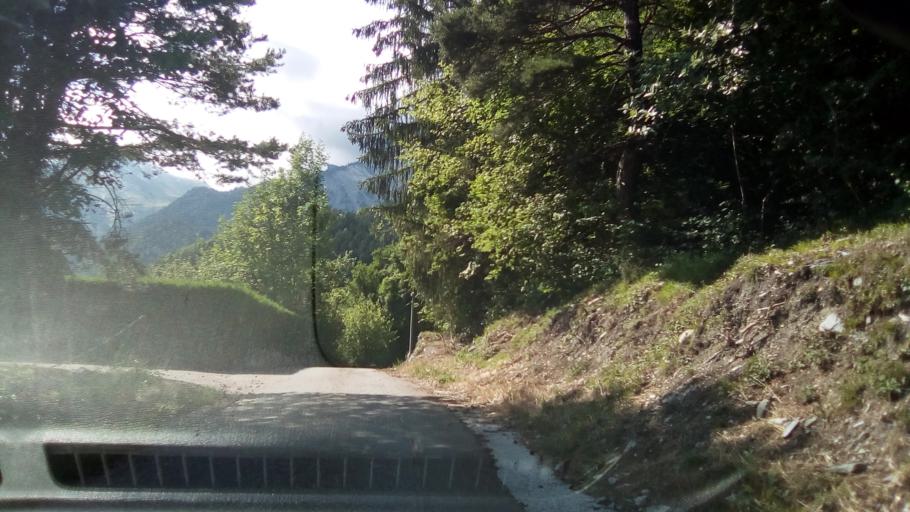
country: CH
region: Valais
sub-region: Conthey District
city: Chamoson
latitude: 46.2133
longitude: 7.2235
